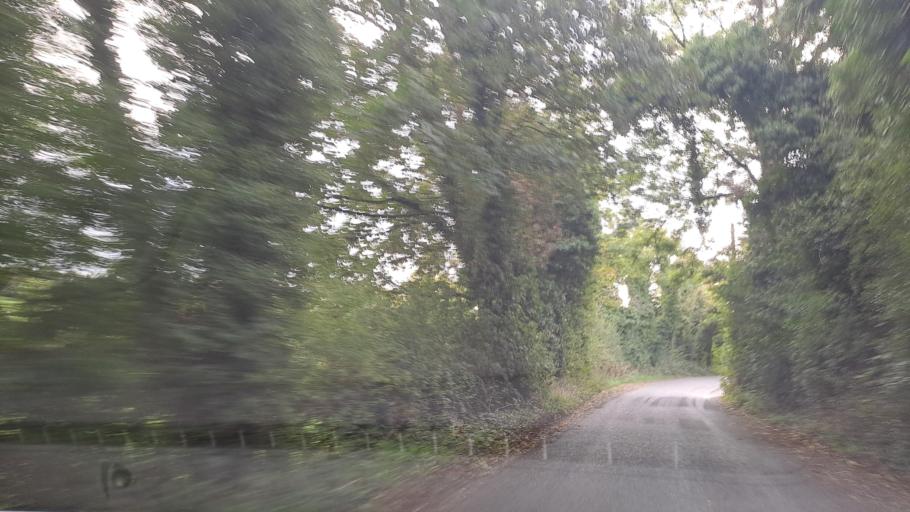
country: IE
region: Ulster
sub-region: An Cabhan
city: Kingscourt
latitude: 53.9556
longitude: -6.7901
